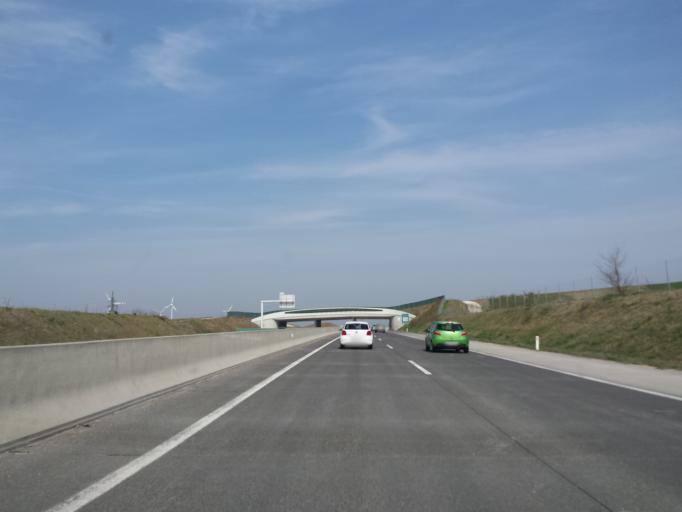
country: AT
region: Lower Austria
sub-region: Politischer Bezirk Mistelbach
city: Gaweinstal
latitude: 48.4983
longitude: 16.5999
